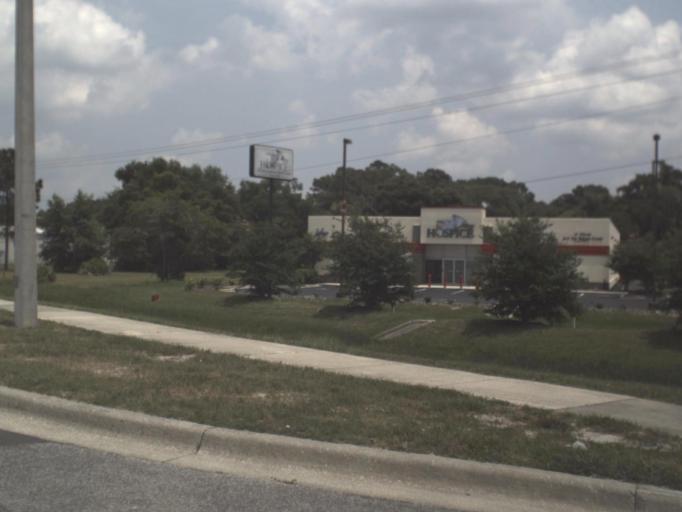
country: US
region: Florida
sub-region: Putnam County
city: Palatka
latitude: 29.6380
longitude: -81.6778
